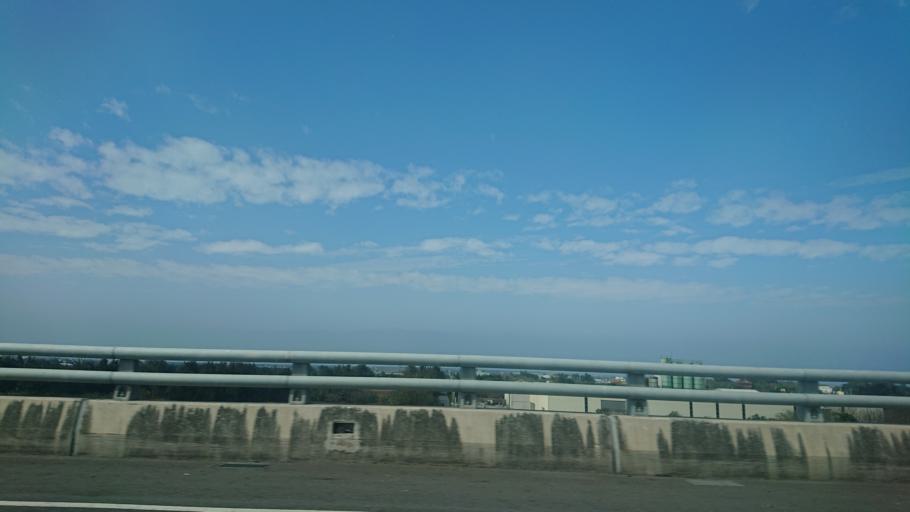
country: TW
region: Taiwan
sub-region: Yunlin
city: Douliu
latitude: 23.8532
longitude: 120.2958
